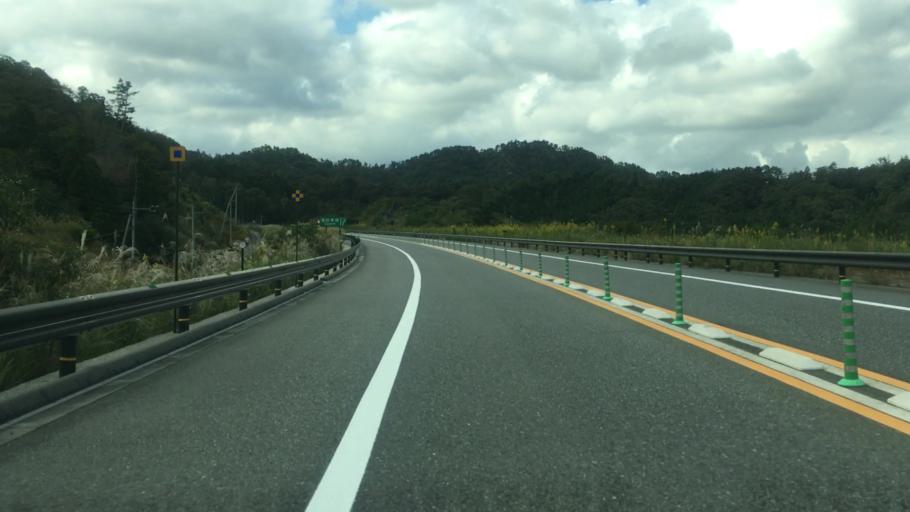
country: JP
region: Hyogo
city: Toyooka
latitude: 35.3293
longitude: 134.8360
